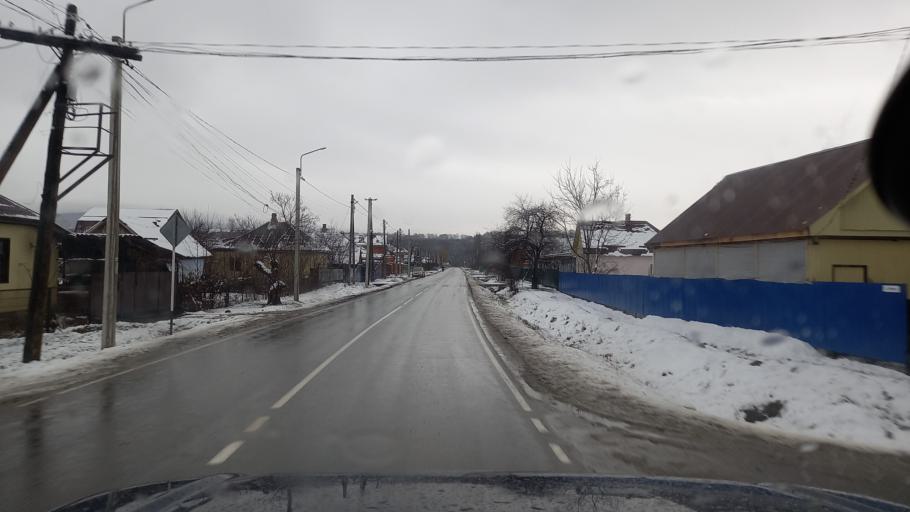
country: RU
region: Adygeya
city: Abadzekhskaya
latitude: 44.3900
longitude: 40.2238
